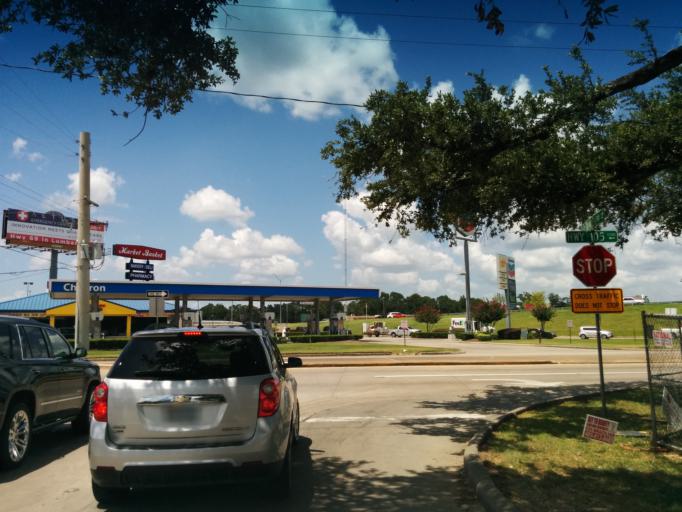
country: US
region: Texas
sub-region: Jefferson County
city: Beaumont
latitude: 30.1331
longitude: -94.1690
